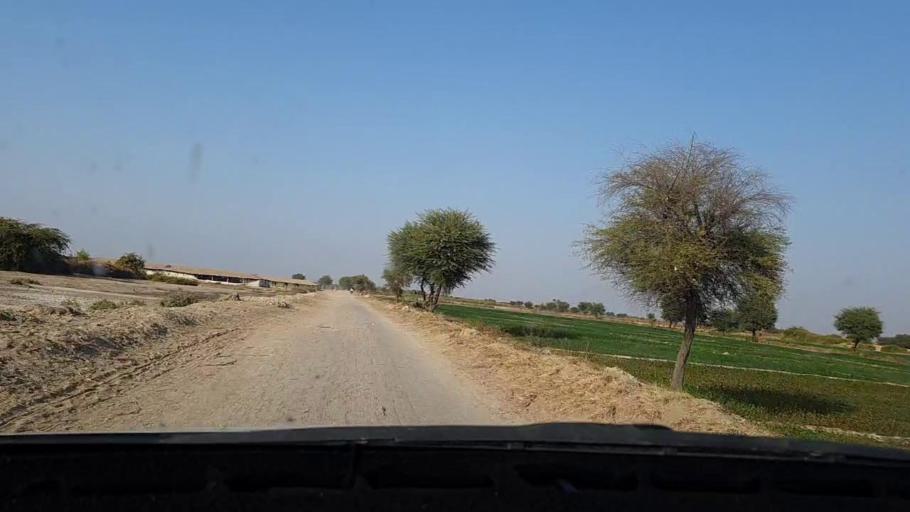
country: PK
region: Sindh
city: Tando Mittha Khan
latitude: 25.8416
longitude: 69.3326
